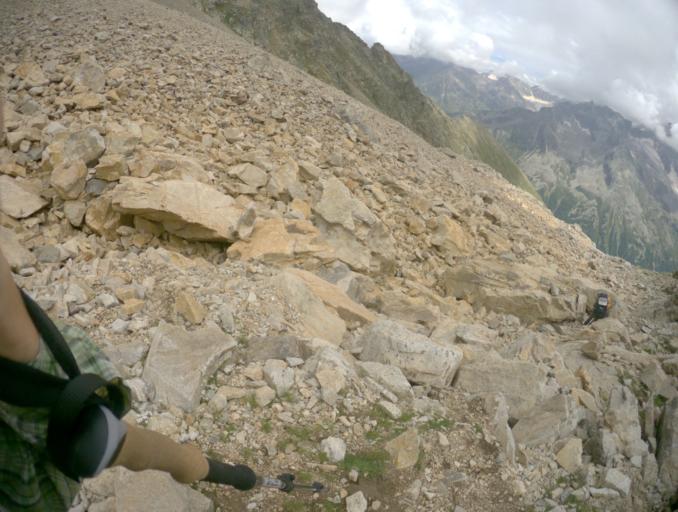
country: RU
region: Karachayevo-Cherkesiya
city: Uchkulan
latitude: 43.2765
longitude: 42.1196
